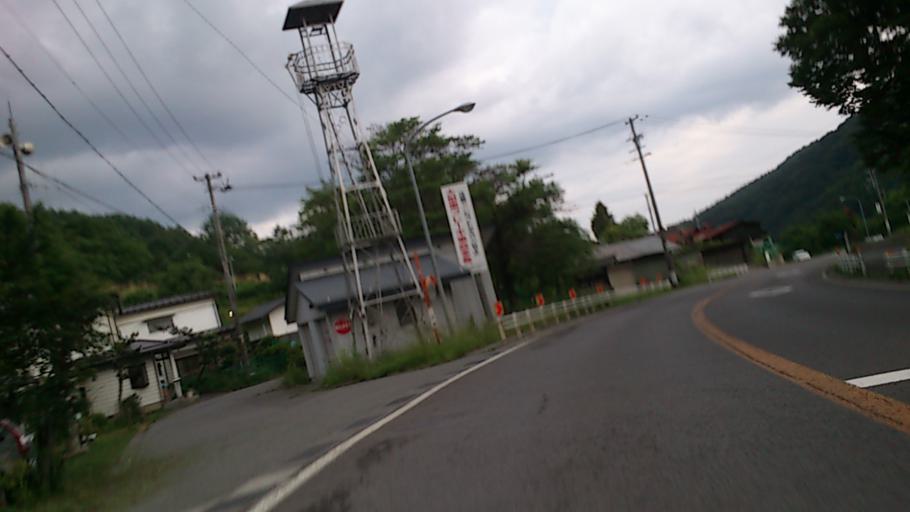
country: JP
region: Nagano
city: Suwa
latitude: 36.1219
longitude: 138.1021
